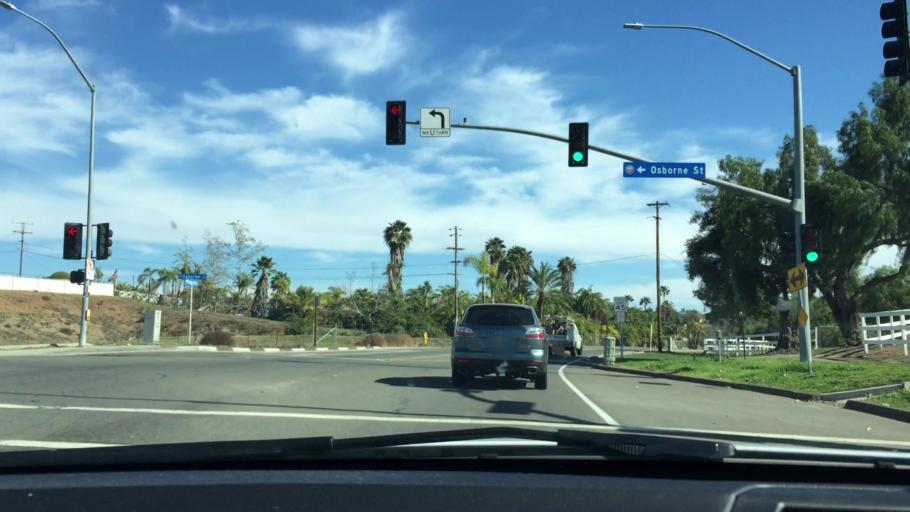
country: US
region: California
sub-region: San Diego County
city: Vista
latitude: 33.2343
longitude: -117.2514
